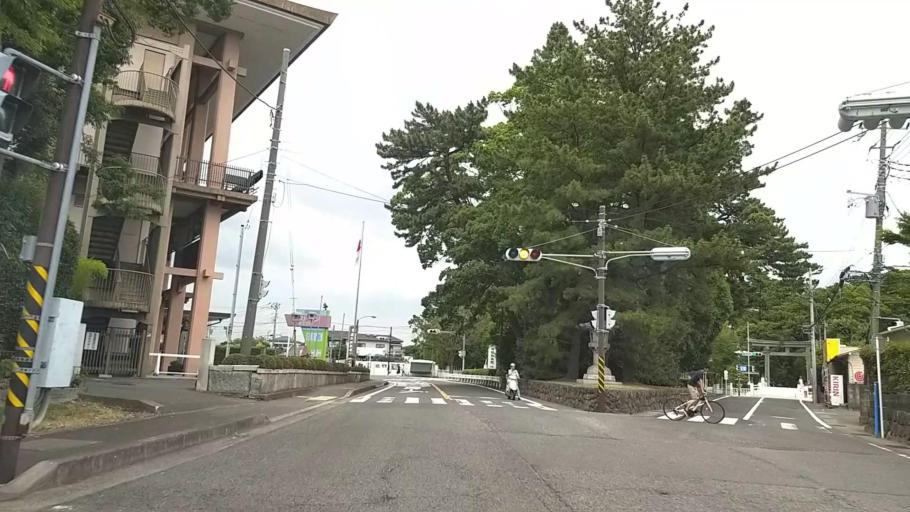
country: JP
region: Kanagawa
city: Chigasaki
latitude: 35.3772
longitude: 139.3811
